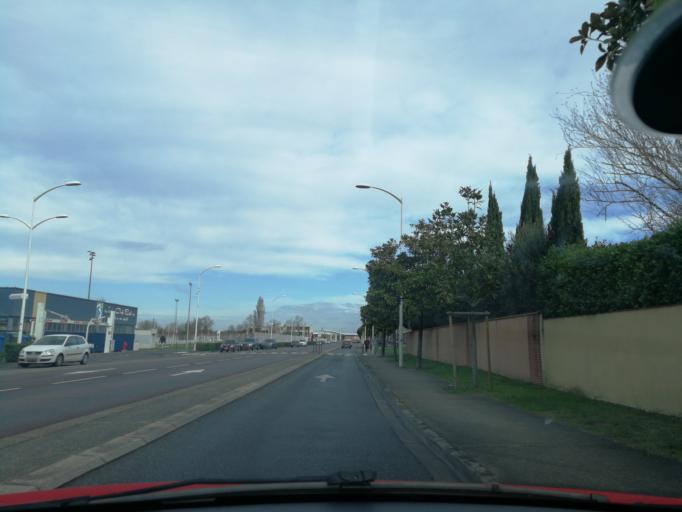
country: FR
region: Midi-Pyrenees
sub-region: Departement de la Haute-Garonne
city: Balma
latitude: 43.6108
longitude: 1.4897
